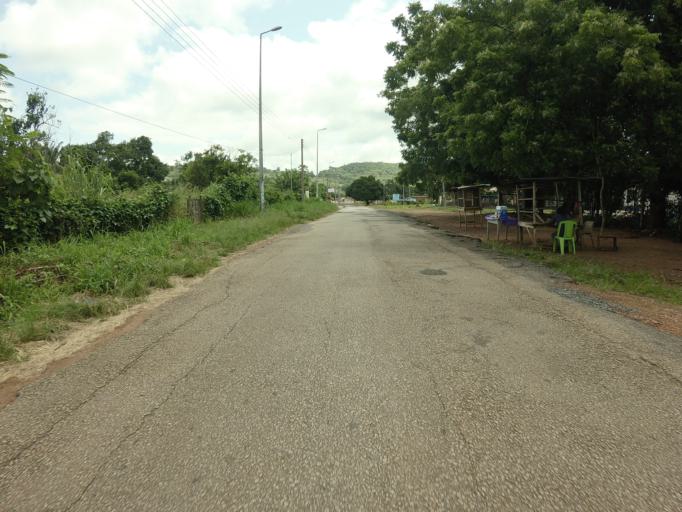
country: GH
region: Volta
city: Ho
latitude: 6.6073
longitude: 0.4611
